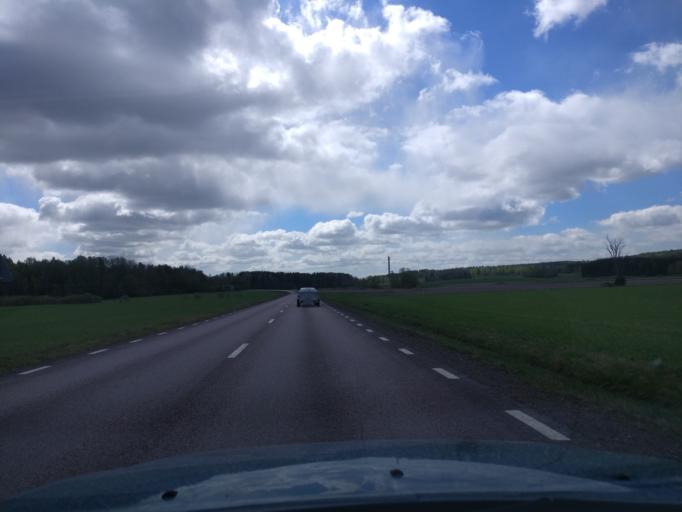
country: SE
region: Vaermland
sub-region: Karlstads Kommun
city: Molkom
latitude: 59.6215
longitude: 13.7301
